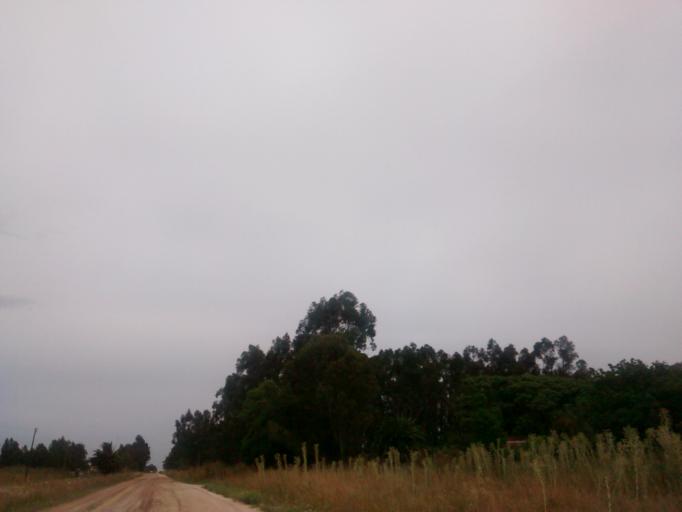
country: AR
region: Buenos Aires
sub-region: Partido de Loberia
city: Loberia
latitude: -38.1905
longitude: -58.7363
